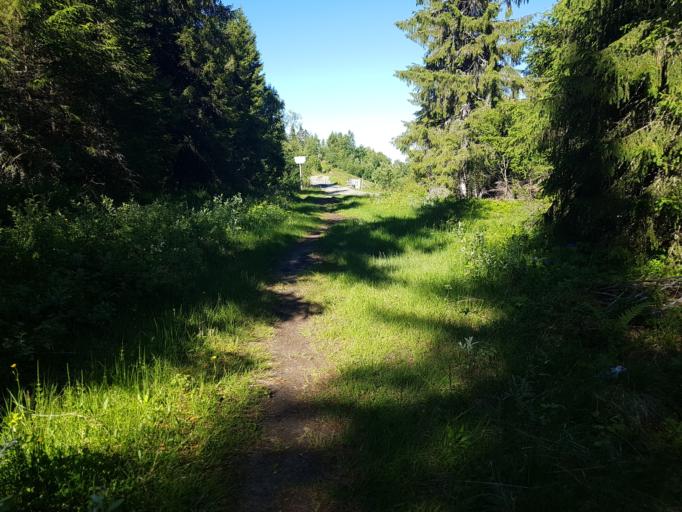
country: NO
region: Sor-Trondelag
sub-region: Trondheim
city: Trondheim
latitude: 63.4357
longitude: 10.2740
